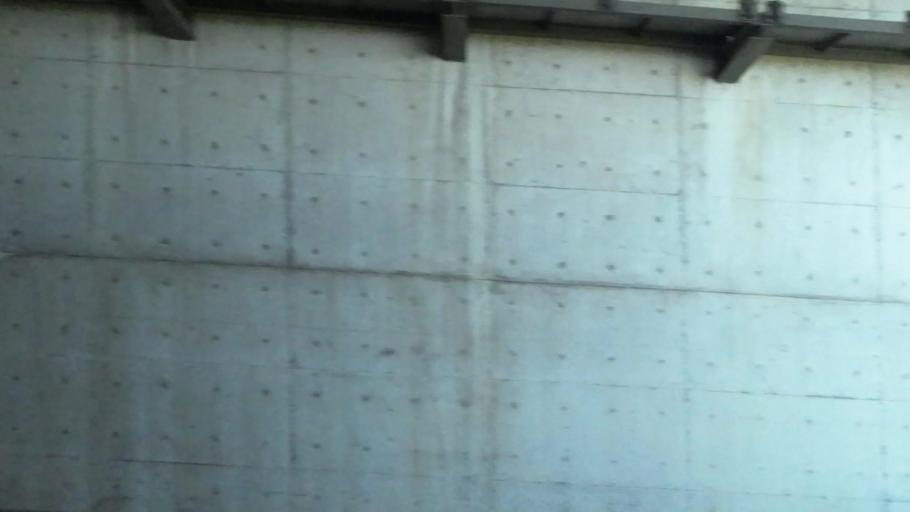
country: JP
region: Kagawa
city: Marugame
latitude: 34.2430
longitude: 133.7811
